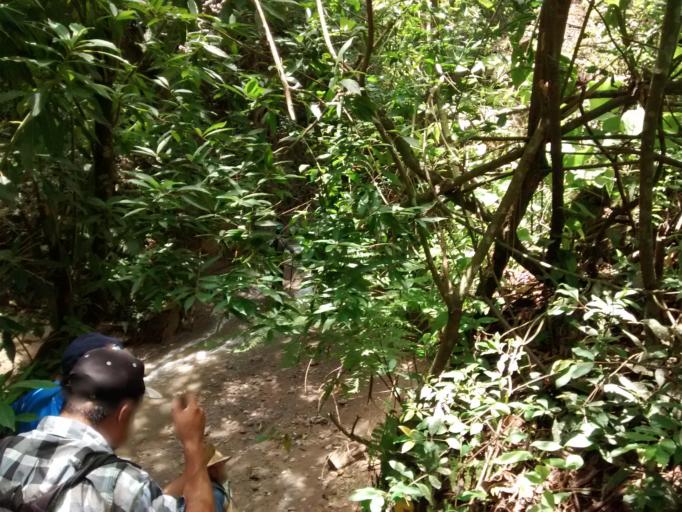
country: GT
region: Sacatepequez
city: Santo Domingo Xenacoj
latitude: 14.6934
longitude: -90.7202
